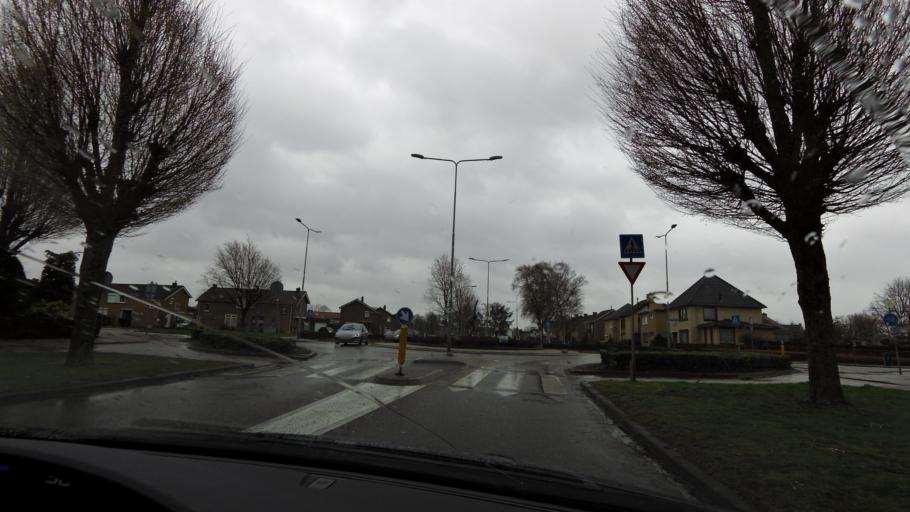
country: NL
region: Limburg
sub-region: Gemeente Stein
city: Stein
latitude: 50.9600
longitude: 5.7694
